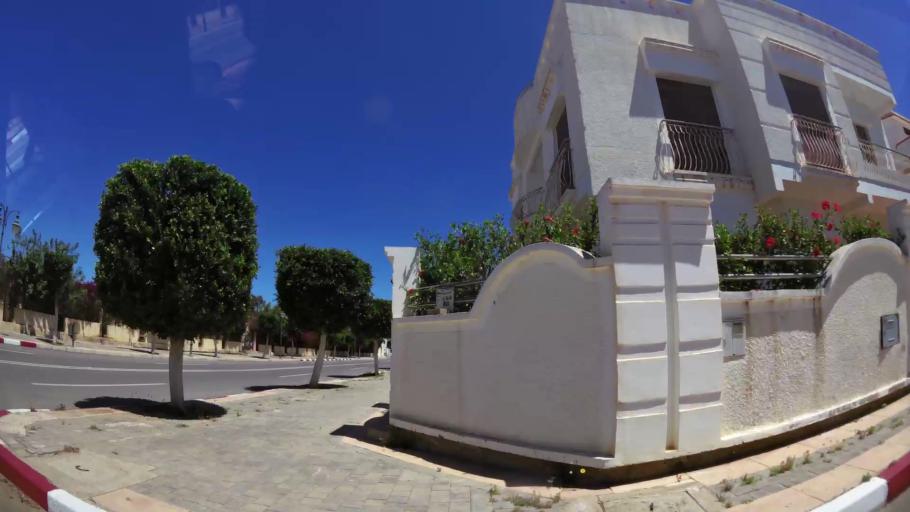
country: MA
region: Oriental
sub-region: Berkane-Taourirt
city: Madagh
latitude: 35.0865
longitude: -2.2414
